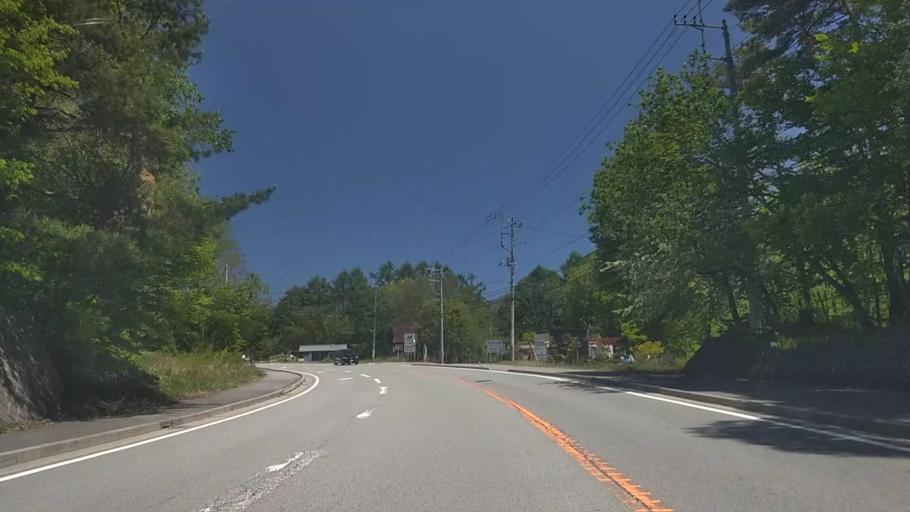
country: JP
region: Yamanashi
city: Nirasaki
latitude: 35.9012
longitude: 138.4429
